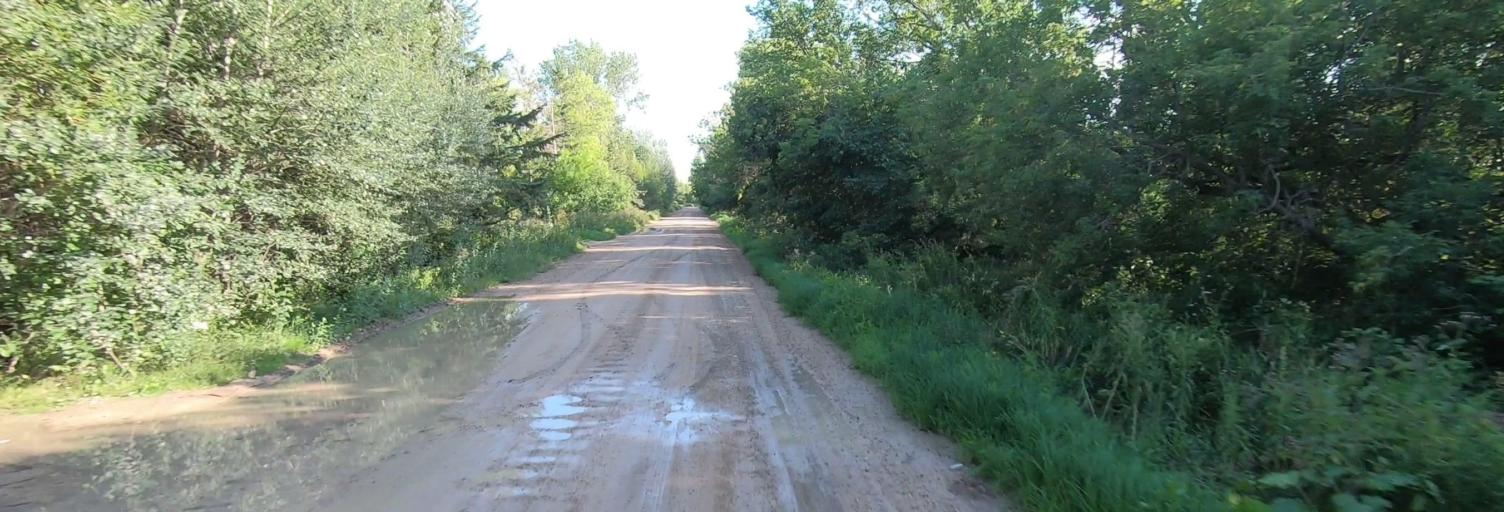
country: CA
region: Manitoba
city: Selkirk
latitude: 50.2740
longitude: -96.8503
